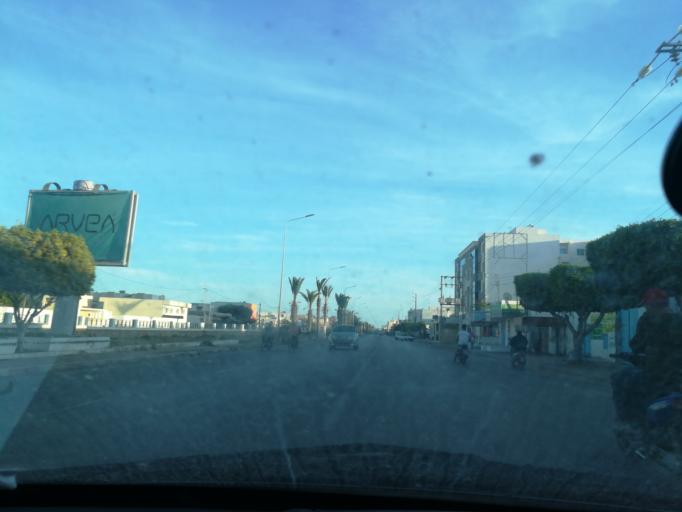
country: TN
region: Safaqis
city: Al Qarmadah
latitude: 34.8182
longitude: 10.7622
